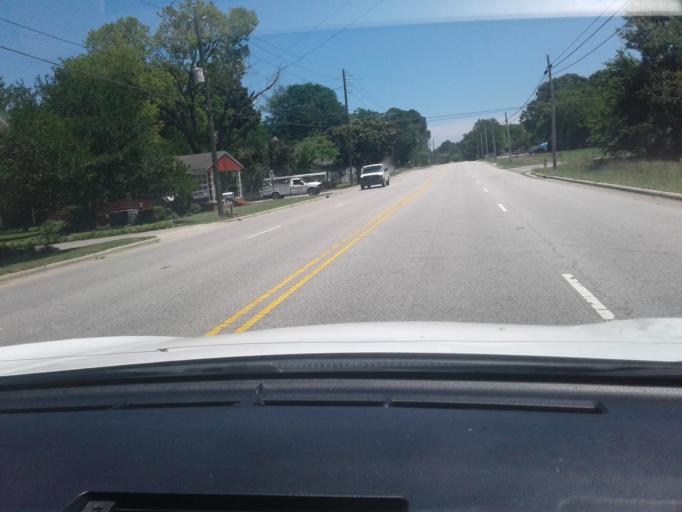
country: US
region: North Carolina
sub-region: Harnett County
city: Lillington
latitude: 35.3931
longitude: -78.8165
